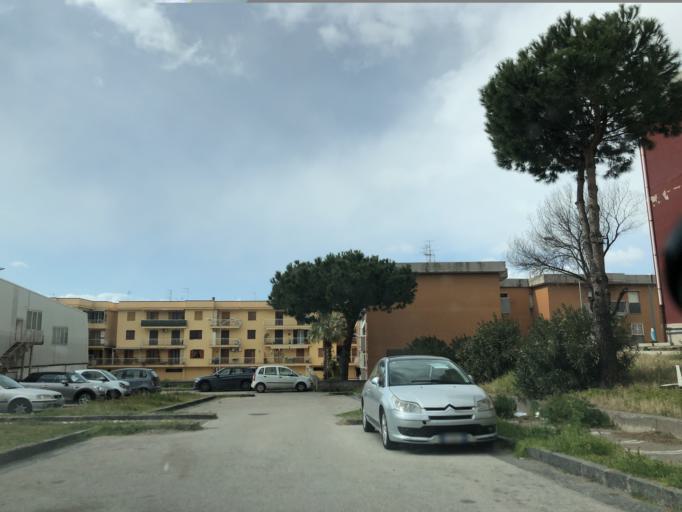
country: IT
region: Campania
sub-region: Provincia di Napoli
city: San Sebastiano al Vesuvio
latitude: 40.8414
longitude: 14.3619
